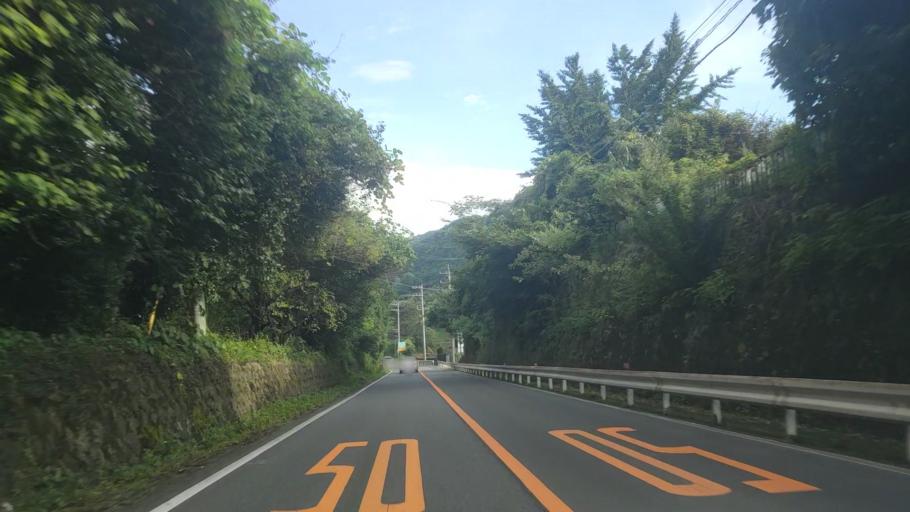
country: JP
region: Gunma
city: Omamacho-omama
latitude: 36.4644
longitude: 139.2584
